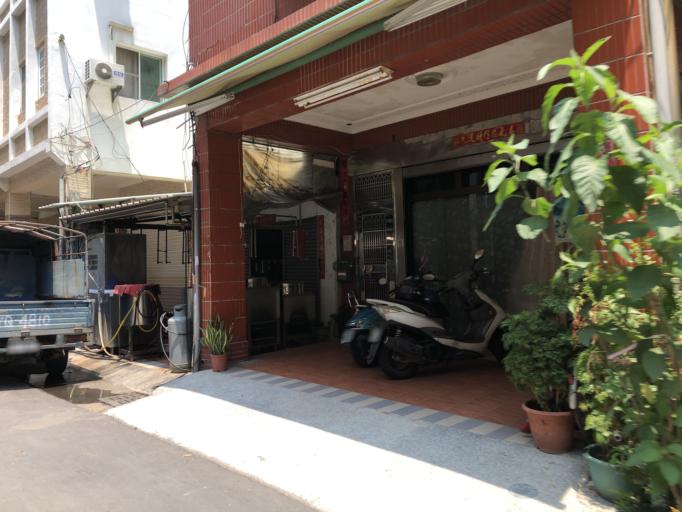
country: TW
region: Kaohsiung
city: Kaohsiung
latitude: 22.6211
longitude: 120.2730
